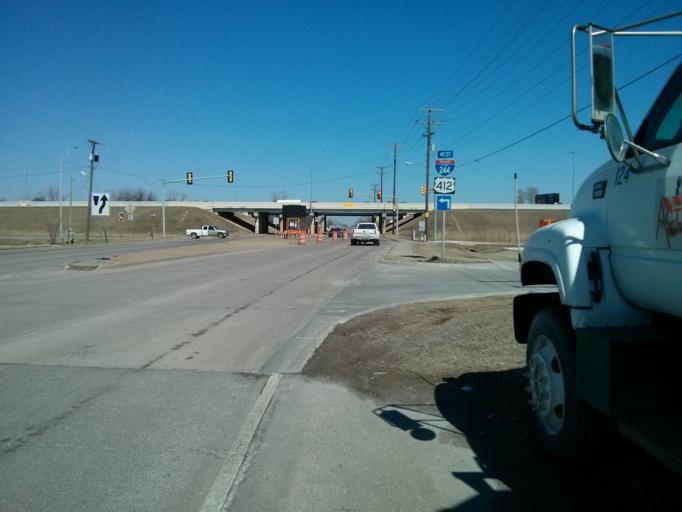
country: US
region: Oklahoma
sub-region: Tulsa County
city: Owasso
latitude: 36.1629
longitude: -95.8686
